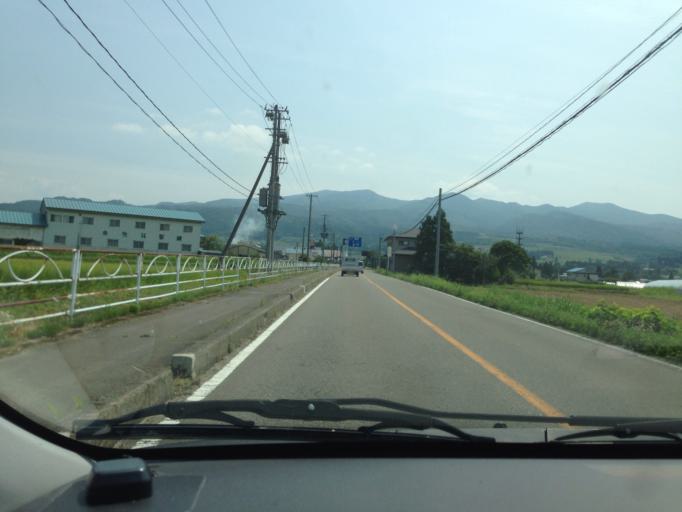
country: JP
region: Fukushima
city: Kitakata
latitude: 37.6436
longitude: 139.9169
